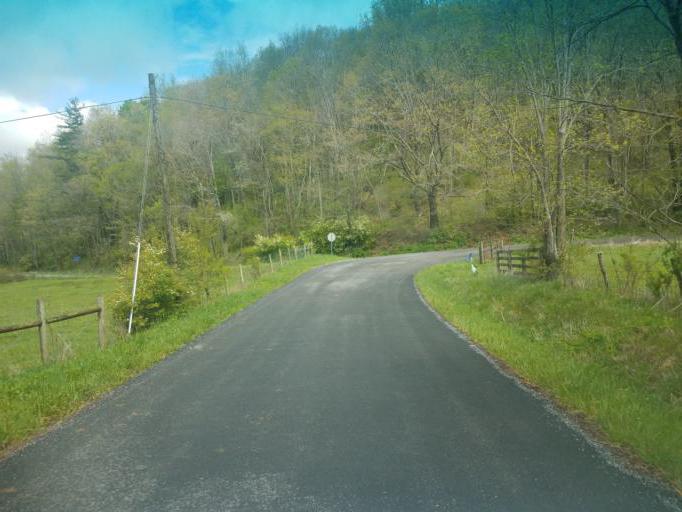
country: US
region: Virginia
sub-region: Smyth County
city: Atkins
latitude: 36.9456
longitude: -81.4166
